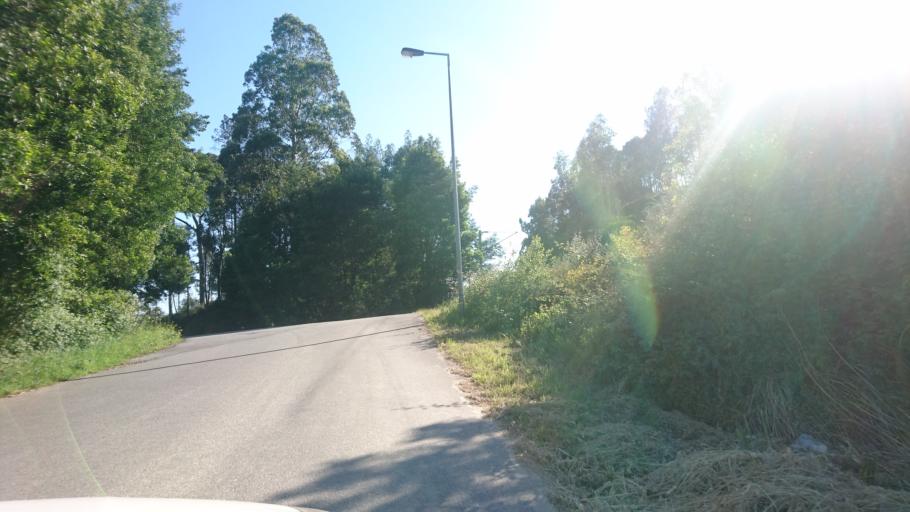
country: PT
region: Porto
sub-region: Paredes
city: Recarei
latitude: 41.1530
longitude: -8.3852
